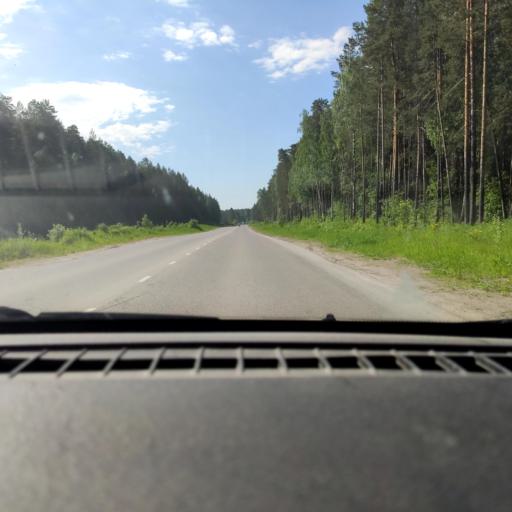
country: RU
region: Perm
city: Overyata
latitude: 58.0031
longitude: 55.8781
